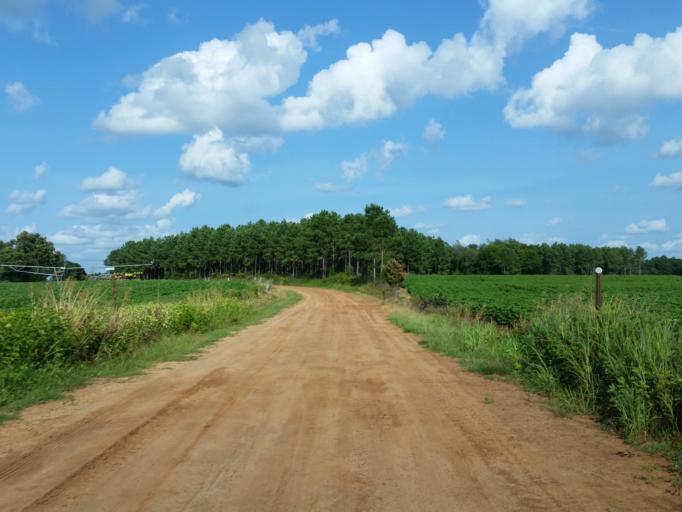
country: US
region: Georgia
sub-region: Lee County
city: Leesburg
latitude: 31.8725
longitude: -84.0515
